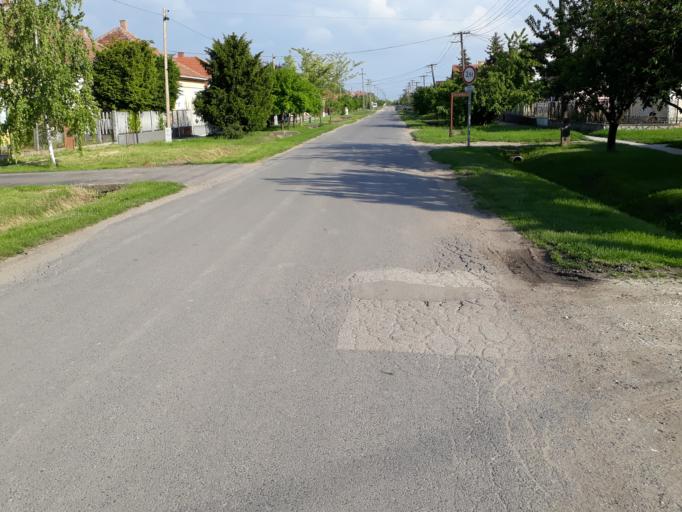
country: HU
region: Jasz-Nagykun-Szolnok
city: Ujszasz
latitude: 47.3126
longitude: 20.1006
